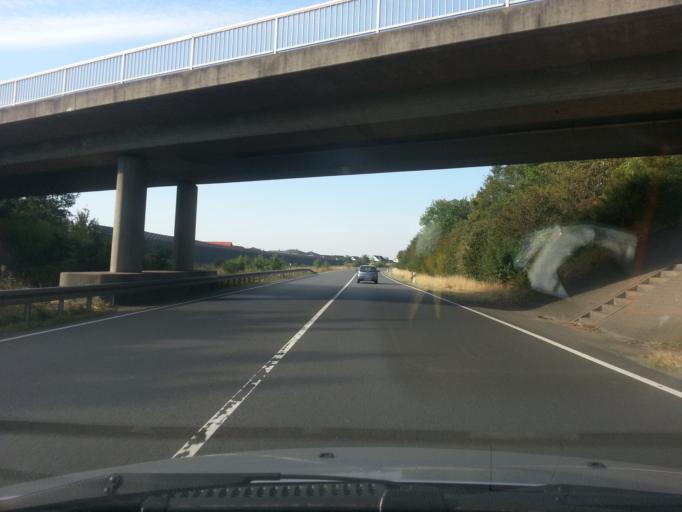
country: DE
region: Hesse
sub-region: Regierungsbezirk Darmstadt
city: Burstadt
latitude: 49.6407
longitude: 8.4764
